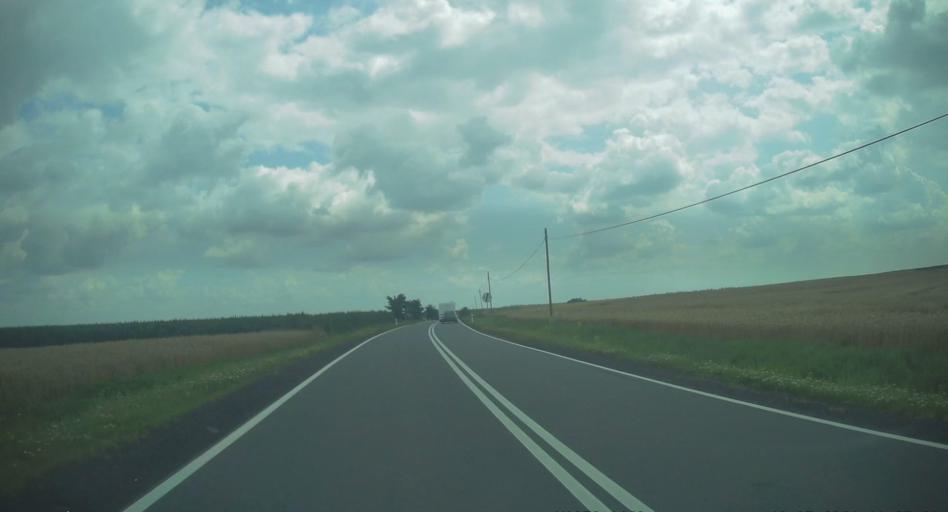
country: PL
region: Opole Voivodeship
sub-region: Powiat prudnicki
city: Raclawice Slaskie
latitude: 50.3544
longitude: 17.7981
